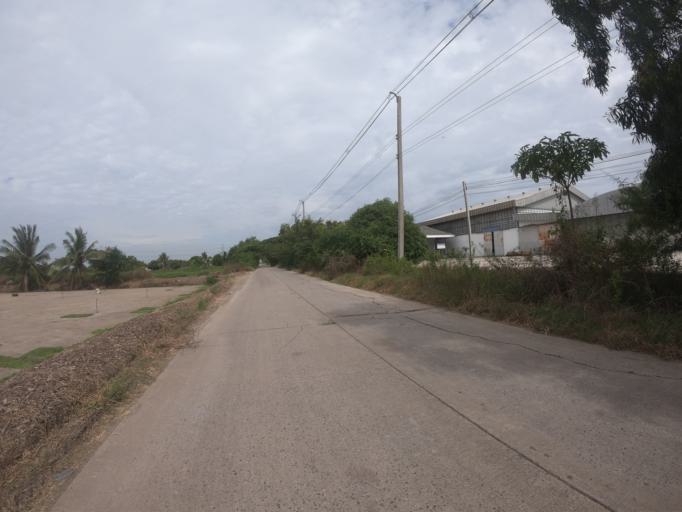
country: TH
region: Pathum Thani
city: Nong Suea
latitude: 14.0319
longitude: 100.8880
